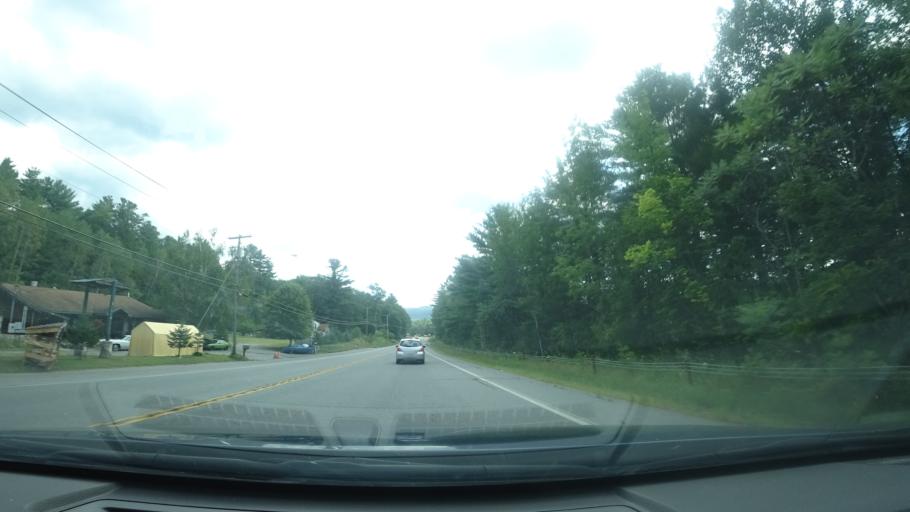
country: US
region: New York
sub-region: Warren County
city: Warrensburg
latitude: 43.5107
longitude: -73.7912
